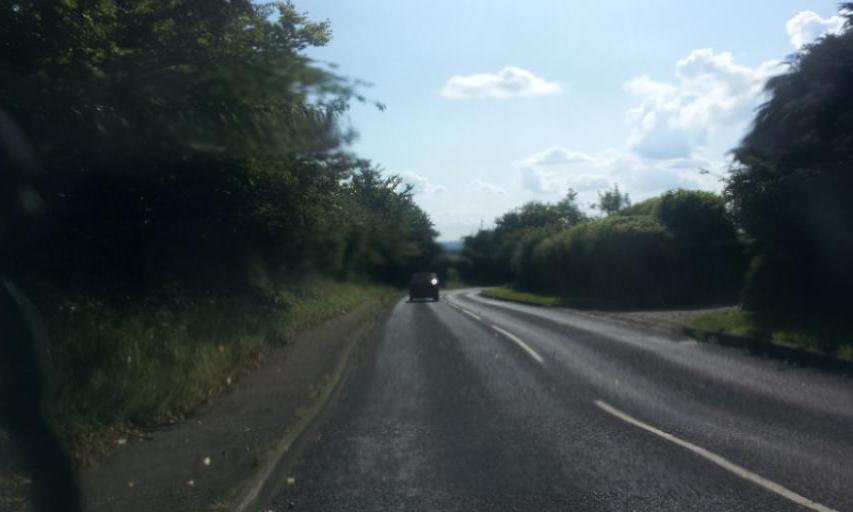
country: GB
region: England
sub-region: Kent
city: Wateringbury
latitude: 51.2597
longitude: 0.4303
